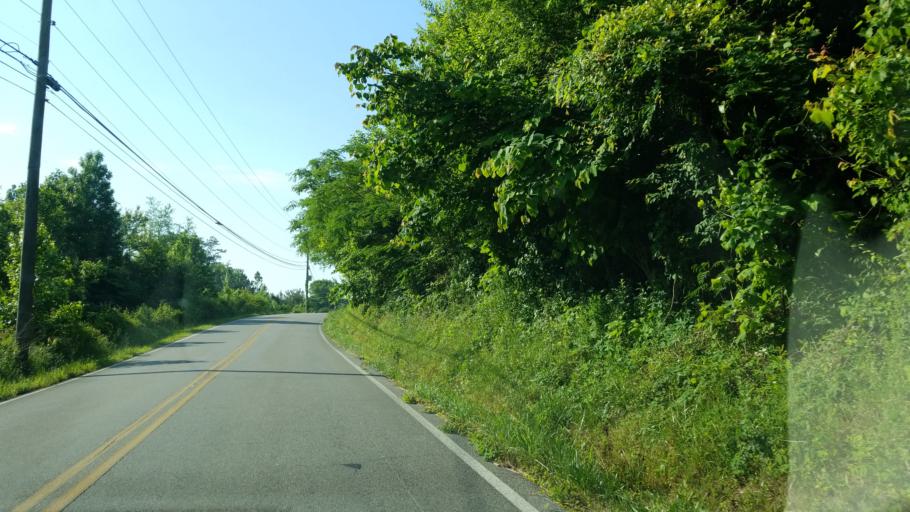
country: US
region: Tennessee
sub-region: Hamilton County
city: Collegedale
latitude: 35.0812
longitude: -85.0087
